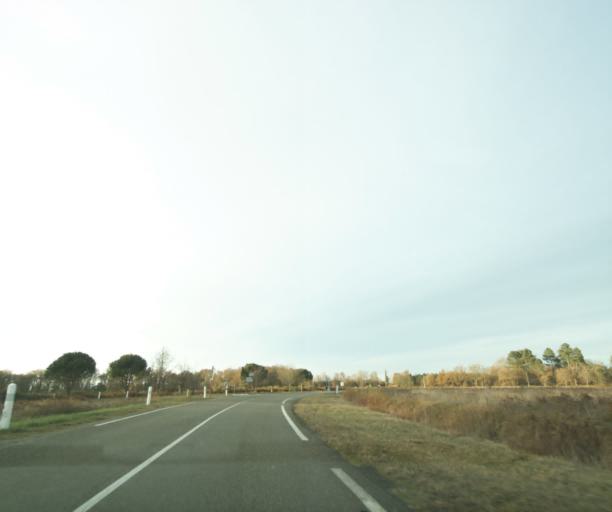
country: FR
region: Aquitaine
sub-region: Departement des Landes
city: Gabarret
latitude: 44.1118
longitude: -0.1016
